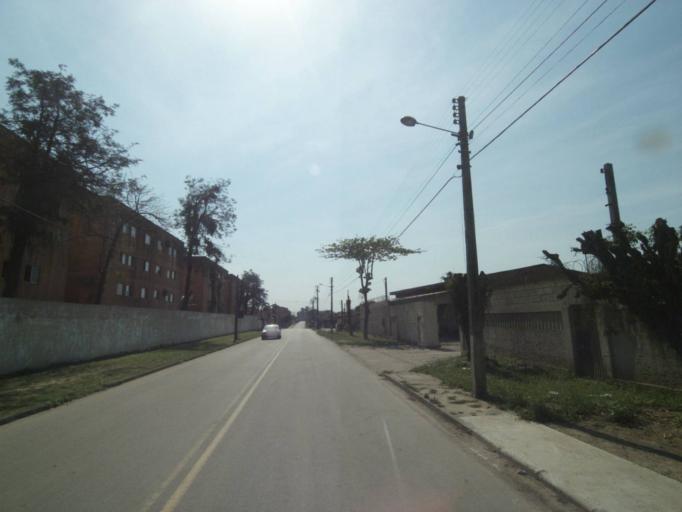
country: BR
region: Parana
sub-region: Paranagua
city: Paranagua
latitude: -25.5499
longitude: -48.5534
